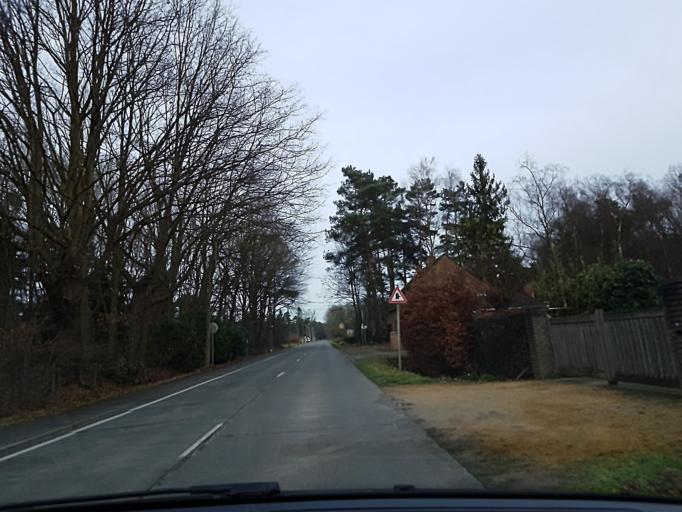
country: BE
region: Flanders
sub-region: Provincie Vlaams-Brabant
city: Keerbergen
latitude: 51.0165
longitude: 4.6008
